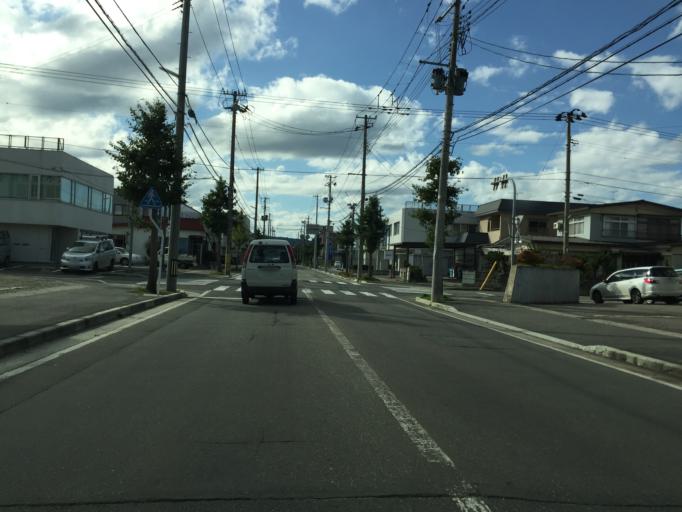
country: JP
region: Yamagata
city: Yonezawa
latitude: 37.9178
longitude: 140.1169
